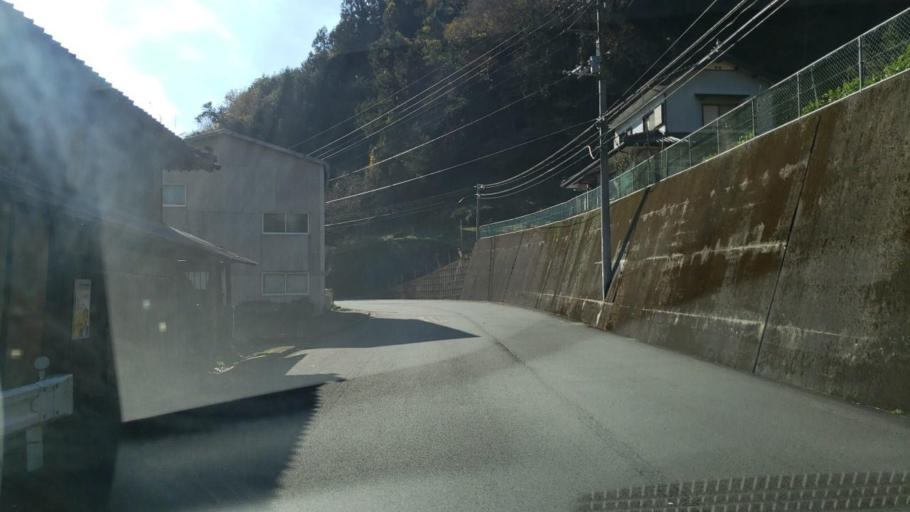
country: JP
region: Tokushima
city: Wakimachi
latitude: 34.0162
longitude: 134.0336
